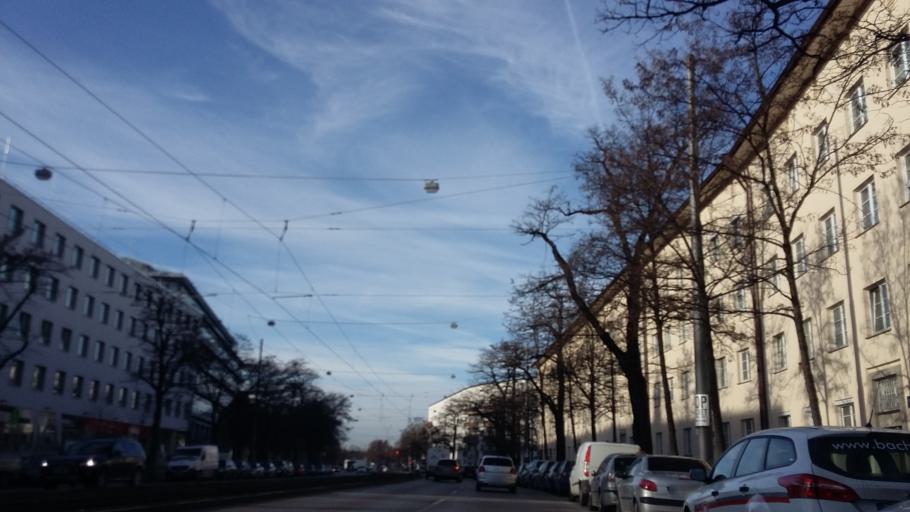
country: DE
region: Bavaria
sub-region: Upper Bavaria
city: Munich
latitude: 48.1494
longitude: 11.5239
